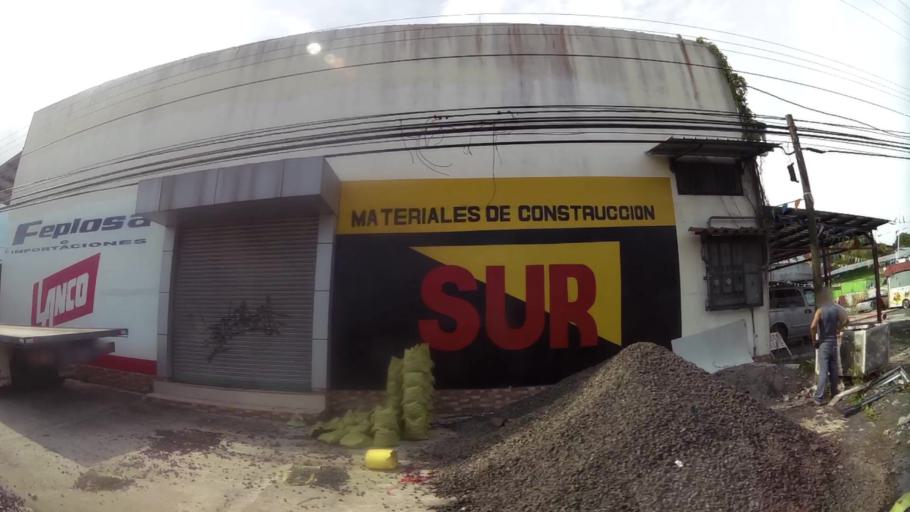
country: PA
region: Panama
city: La Chorrera
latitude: 8.8845
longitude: -79.7747
